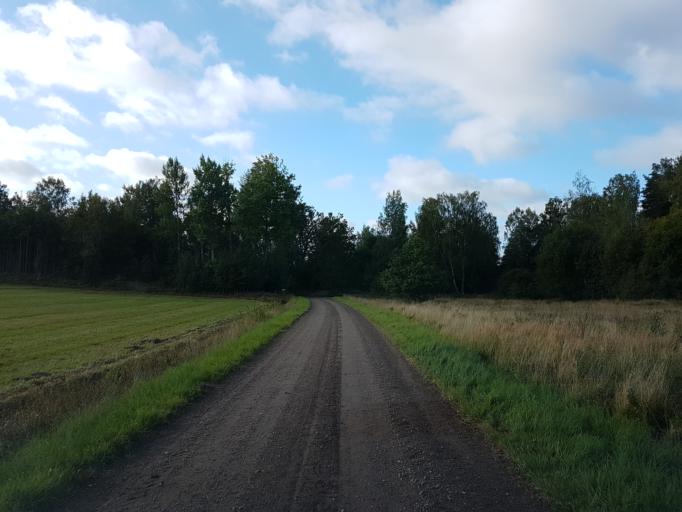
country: SE
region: OEstergoetland
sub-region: Atvidabergs Kommun
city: Atvidaberg
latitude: 58.2165
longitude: 15.9892
